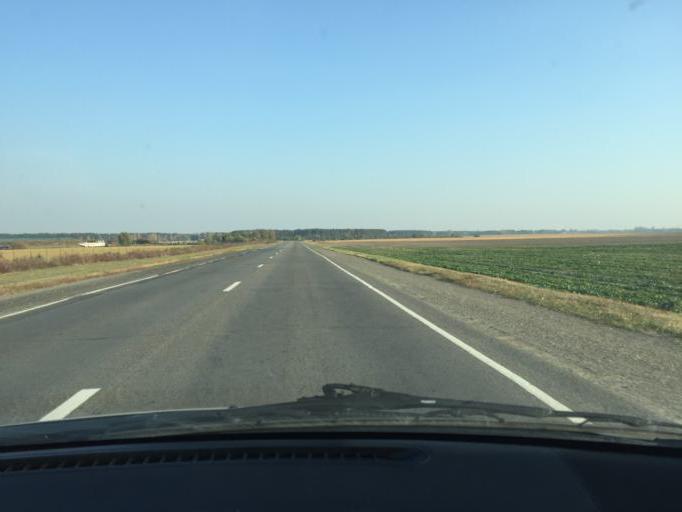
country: BY
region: Brest
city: Davyd-Haradok
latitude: 52.2519
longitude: 27.0606
